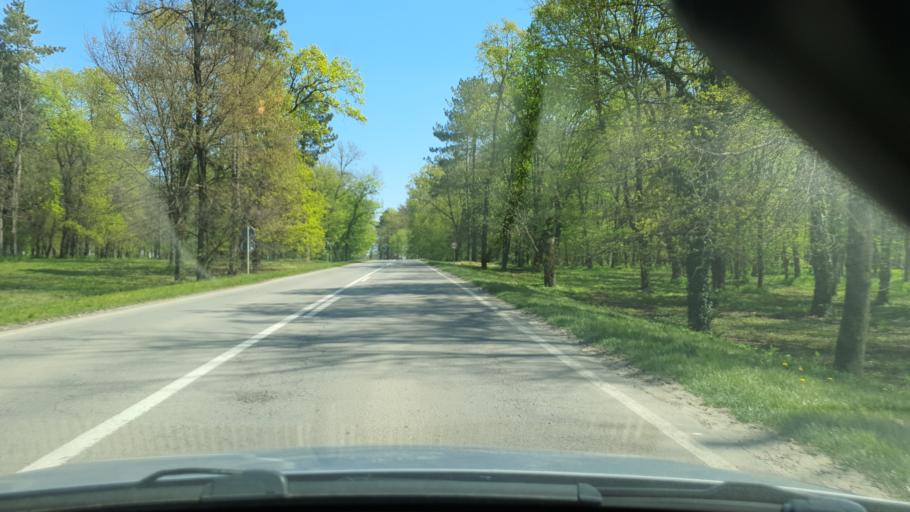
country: RS
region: Autonomna Pokrajina Vojvodina
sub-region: Zapadnobacki Okrug
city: Sombor
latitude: 45.7546
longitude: 19.1134
